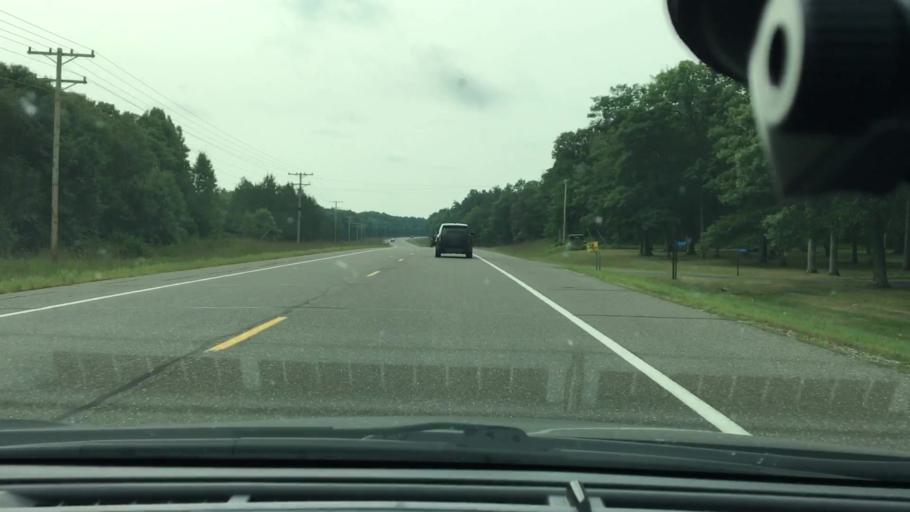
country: US
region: Minnesota
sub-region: Crow Wing County
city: Cross Lake
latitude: 46.6091
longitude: -94.1318
